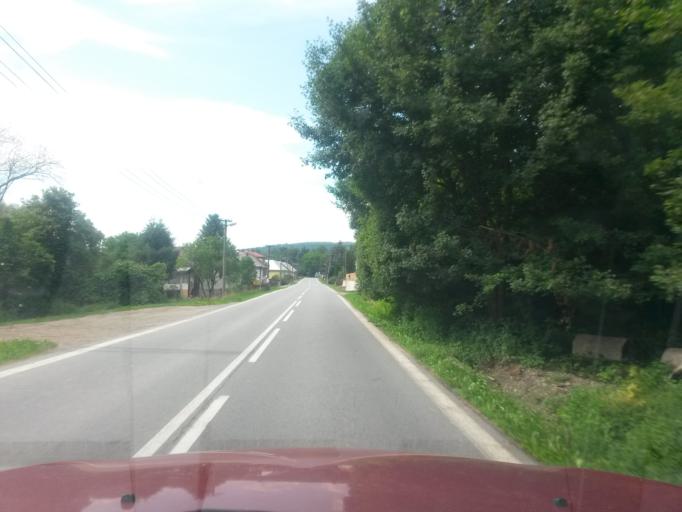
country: SK
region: Presovsky
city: Snina
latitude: 48.9936
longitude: 22.2373
